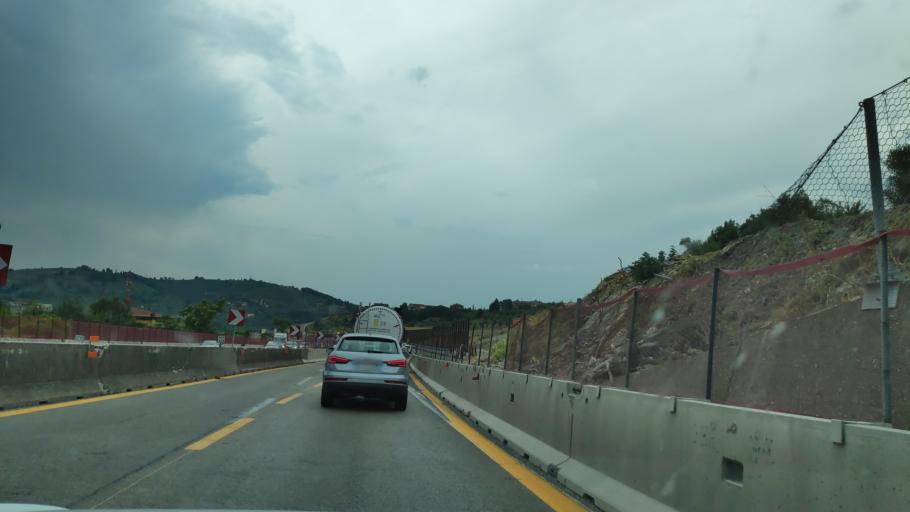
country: IT
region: Tuscany
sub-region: Province of Florence
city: Grassina Ponte a Ema
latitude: 43.7323
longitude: 11.3114
